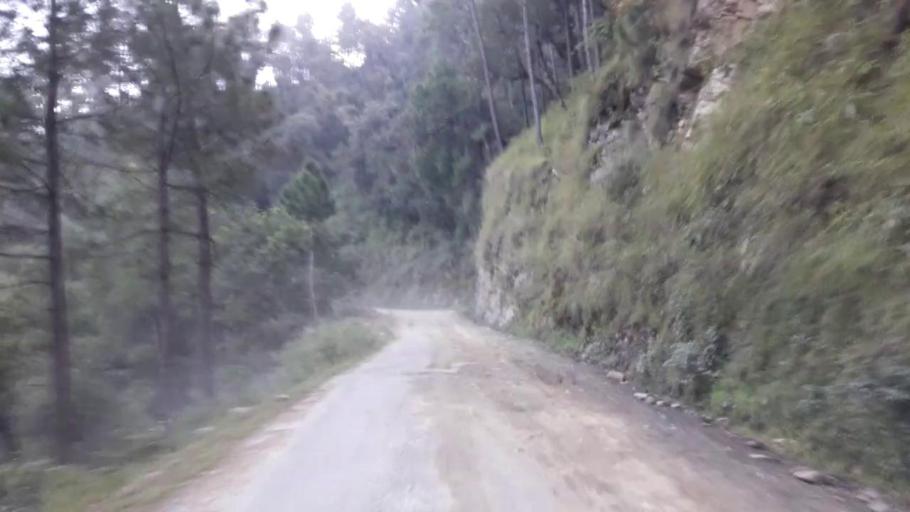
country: IN
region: Himachal Pradesh
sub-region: Shimla
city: Shimla
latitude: 31.0644
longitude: 77.1494
